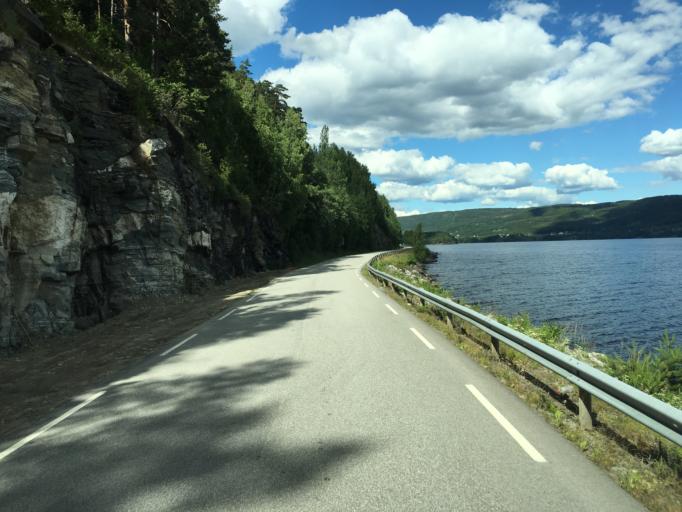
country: NO
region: Oppland
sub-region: Sondre Land
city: Hov
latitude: 60.6028
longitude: 10.3240
